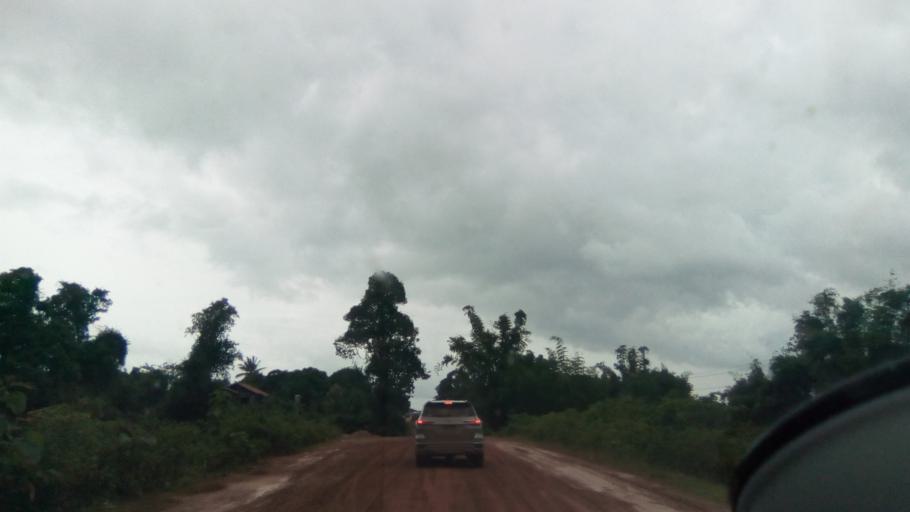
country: LA
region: Attapu
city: Attapu
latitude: 14.7436
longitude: 106.6945
